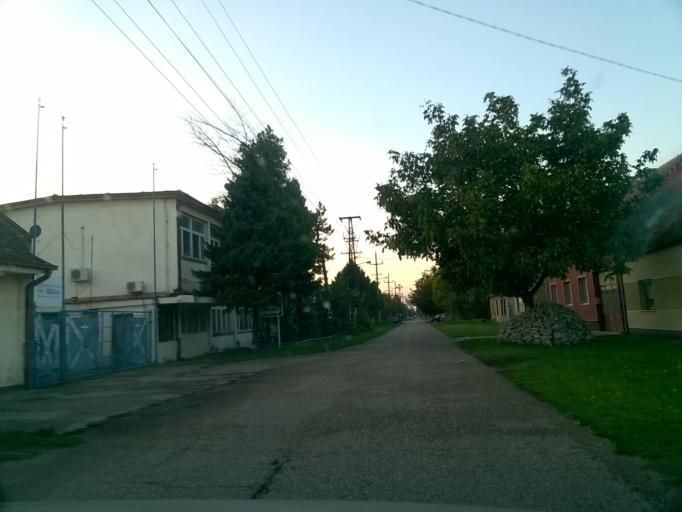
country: RS
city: Crepaja
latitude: 44.9625
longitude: 20.6920
